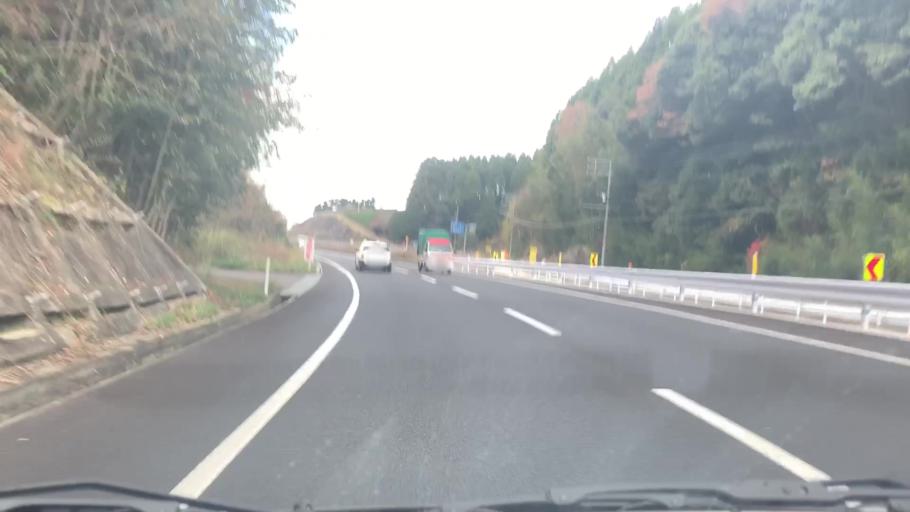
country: JP
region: Saga Prefecture
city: Takeocho-takeo
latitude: 33.2622
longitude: 129.9712
